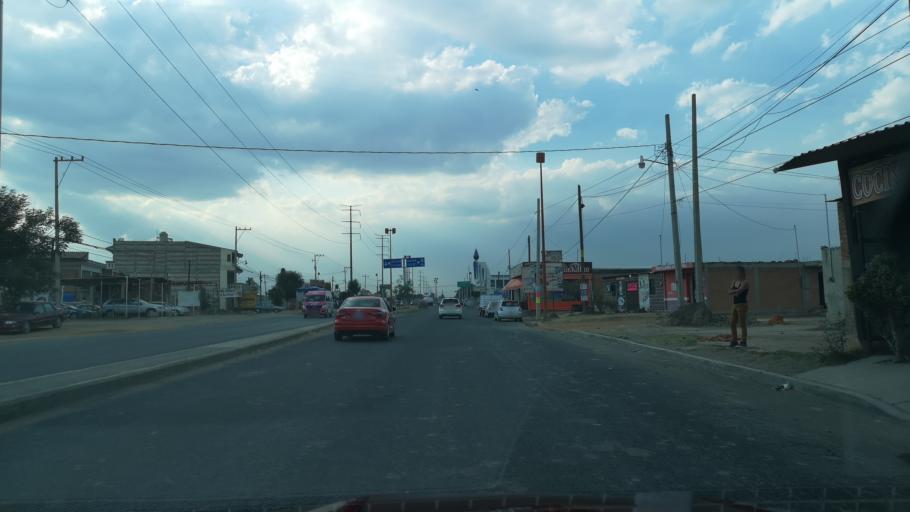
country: MX
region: Puebla
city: Cuanala
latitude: 19.0829
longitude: -98.3293
